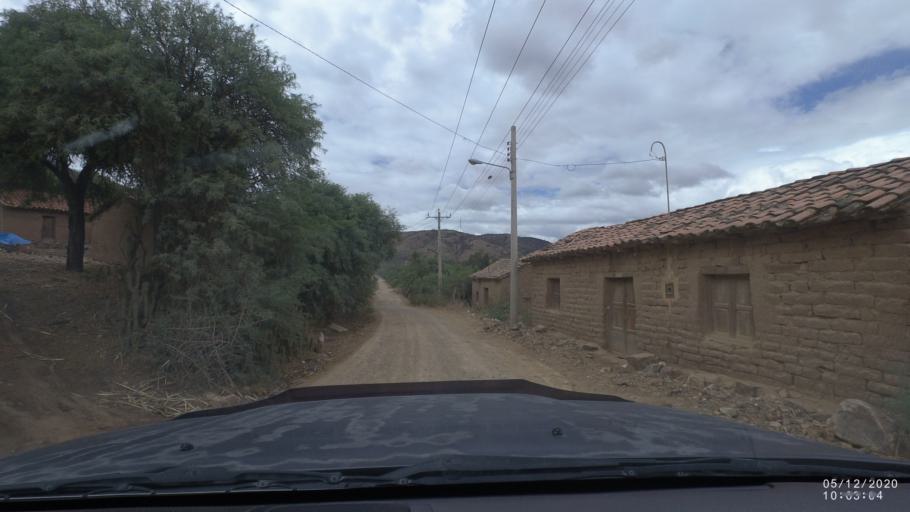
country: BO
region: Cochabamba
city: Sipe Sipe
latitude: -17.4549
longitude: -66.2865
